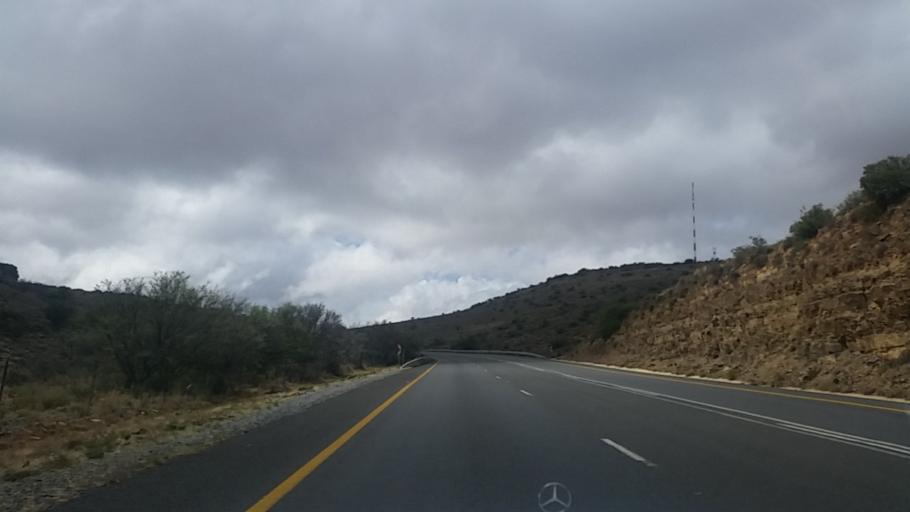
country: ZA
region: Eastern Cape
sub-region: Cacadu District Municipality
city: Graaff-Reinet
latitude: -31.9659
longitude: 24.7224
